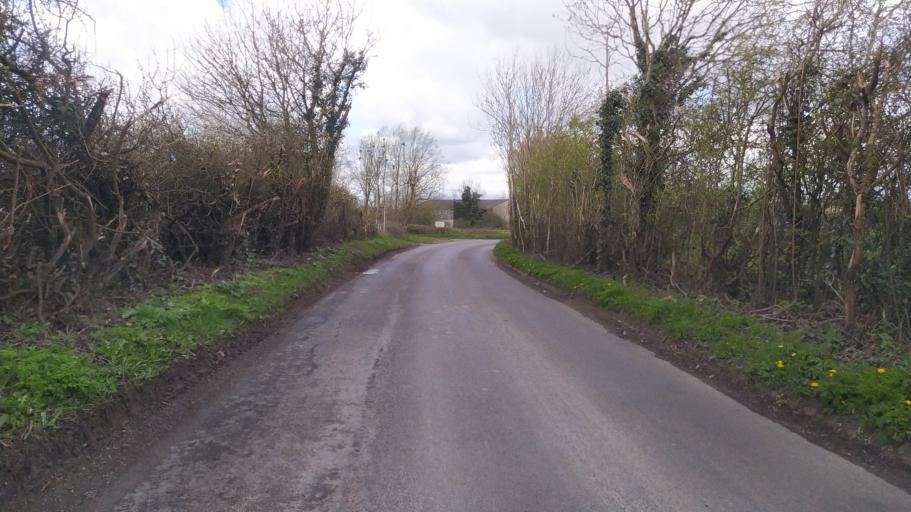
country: GB
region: England
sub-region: Wiltshire
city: Bratton
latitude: 51.2880
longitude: -2.1535
